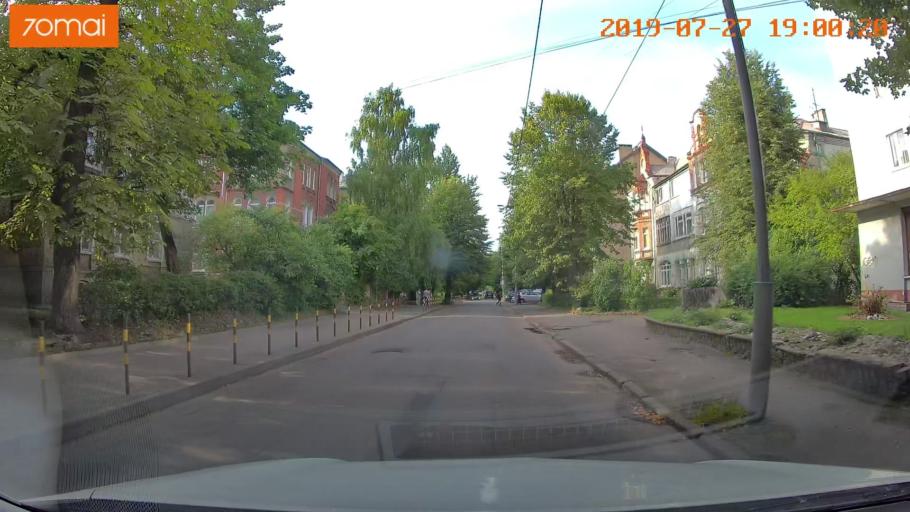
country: RU
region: Kaliningrad
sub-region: Gorod Kaliningrad
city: Kaliningrad
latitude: 54.7263
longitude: 20.4846
